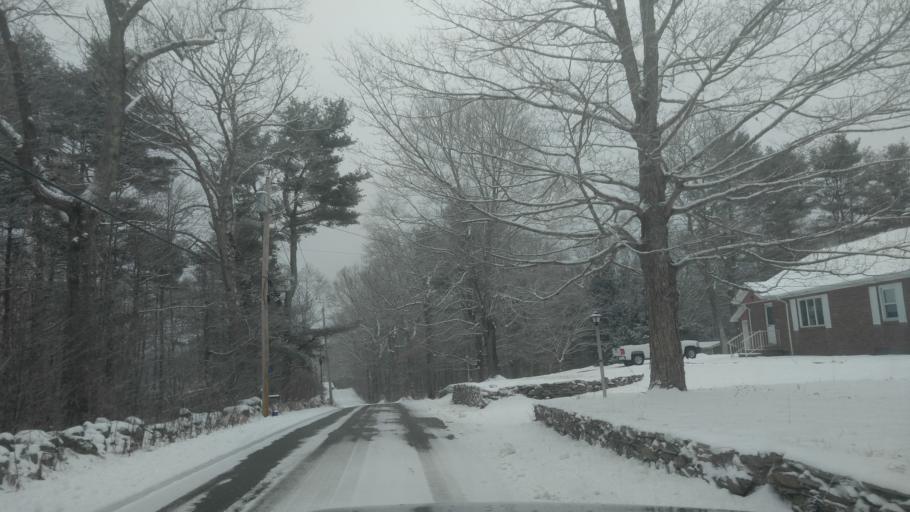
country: US
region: Rhode Island
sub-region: Providence County
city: Foster
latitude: 41.8231
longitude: -71.7226
